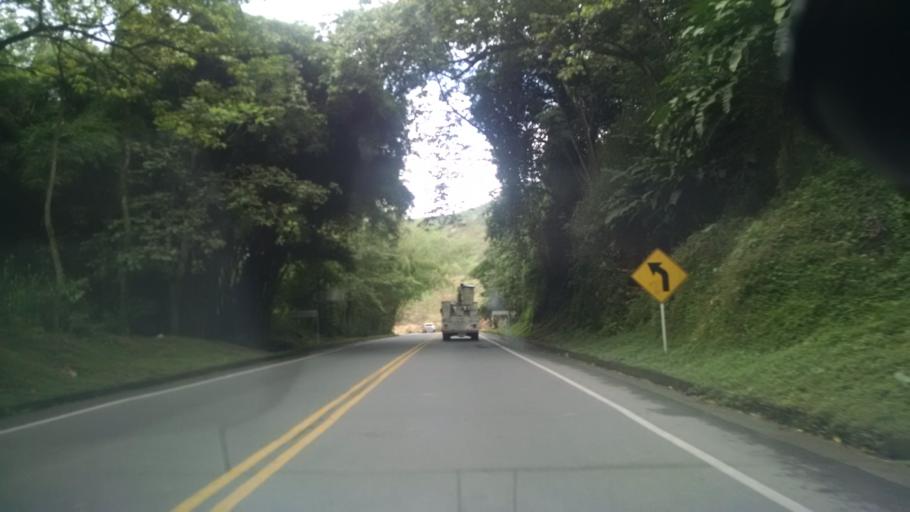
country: CO
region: Caldas
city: Palestina
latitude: 5.0613
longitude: -75.6106
